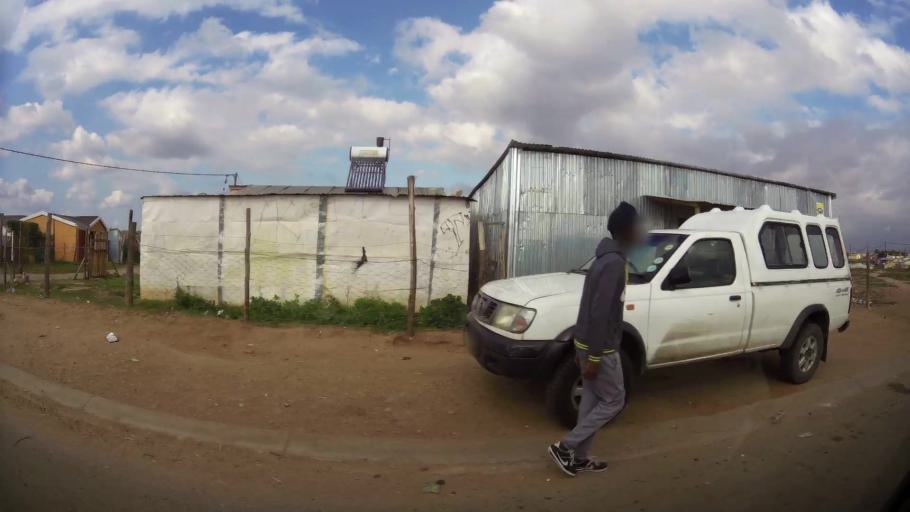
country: ZA
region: Eastern Cape
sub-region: Nelson Mandela Bay Metropolitan Municipality
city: Uitenhage
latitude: -33.7457
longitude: 25.3964
